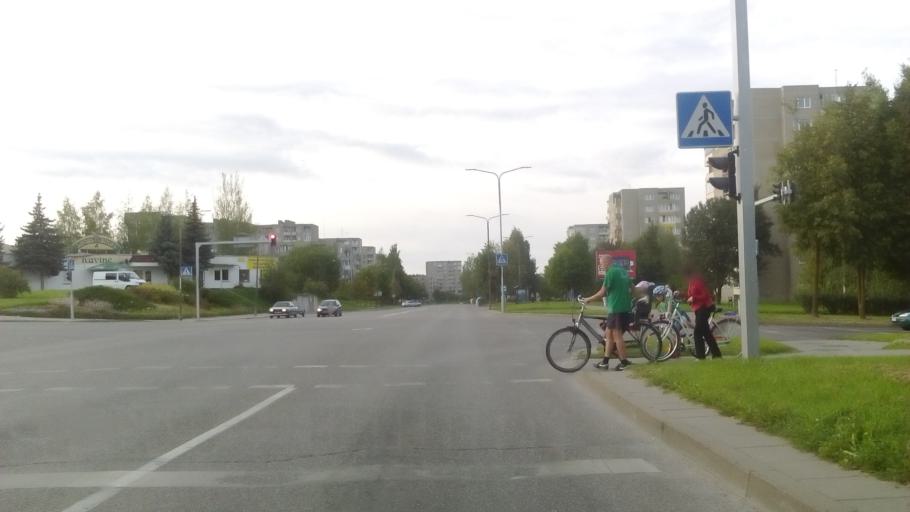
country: LT
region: Alytaus apskritis
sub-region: Alytus
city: Alytus
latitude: 54.3937
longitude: 24.0185
